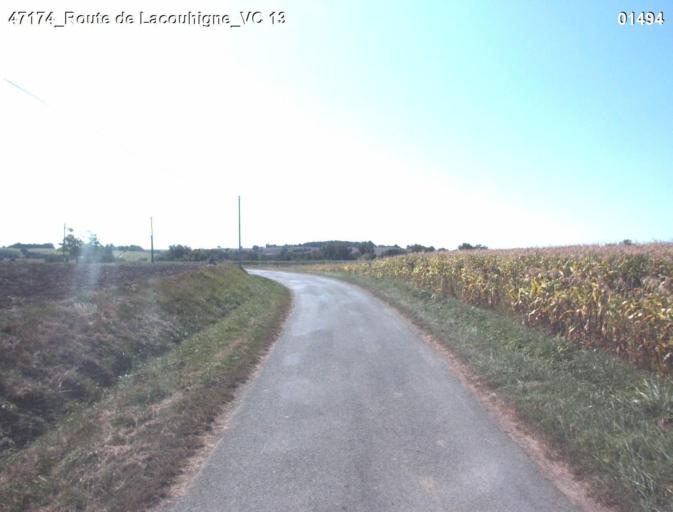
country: FR
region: Midi-Pyrenees
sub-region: Departement du Gers
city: Condom
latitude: 44.0251
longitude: 0.3774
